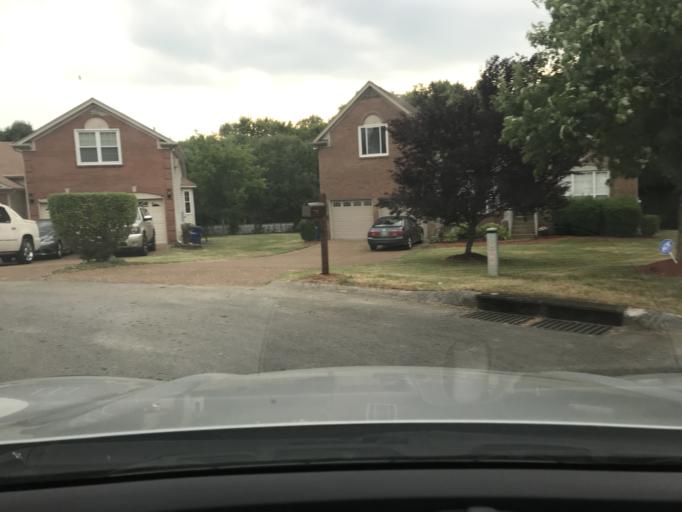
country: US
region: Tennessee
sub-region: Davidson County
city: Goodlettsville
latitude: 36.2990
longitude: -86.7172
